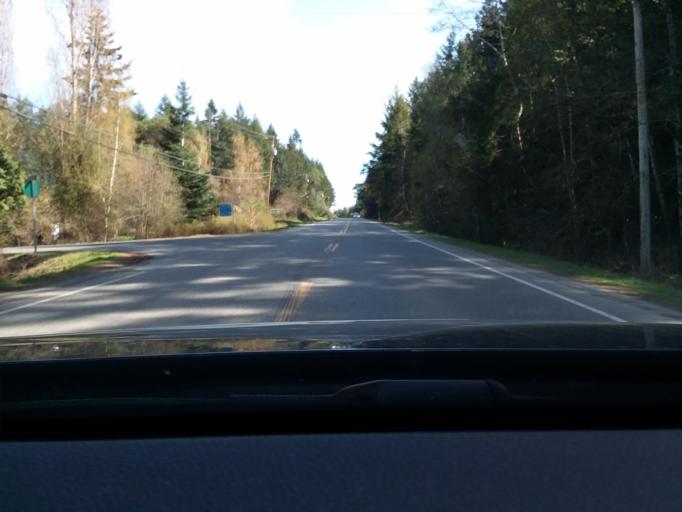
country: CA
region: British Columbia
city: North Cowichan
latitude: 48.8603
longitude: -123.4872
